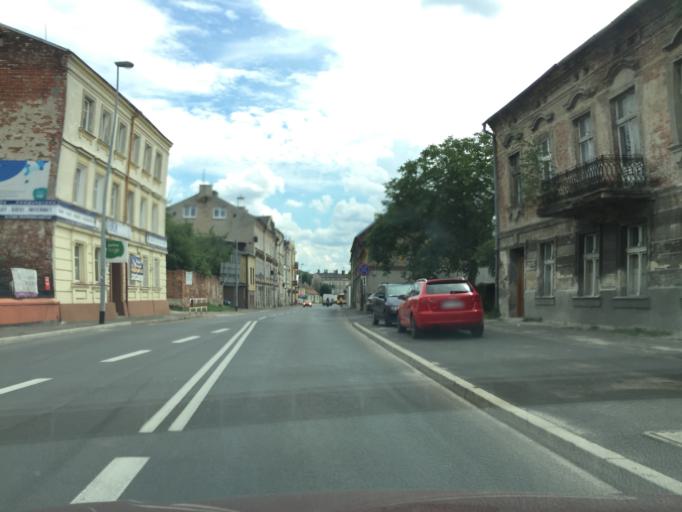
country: PL
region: Greater Poland Voivodeship
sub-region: Kalisz
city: Kalisz
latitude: 51.7702
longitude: 18.0952
